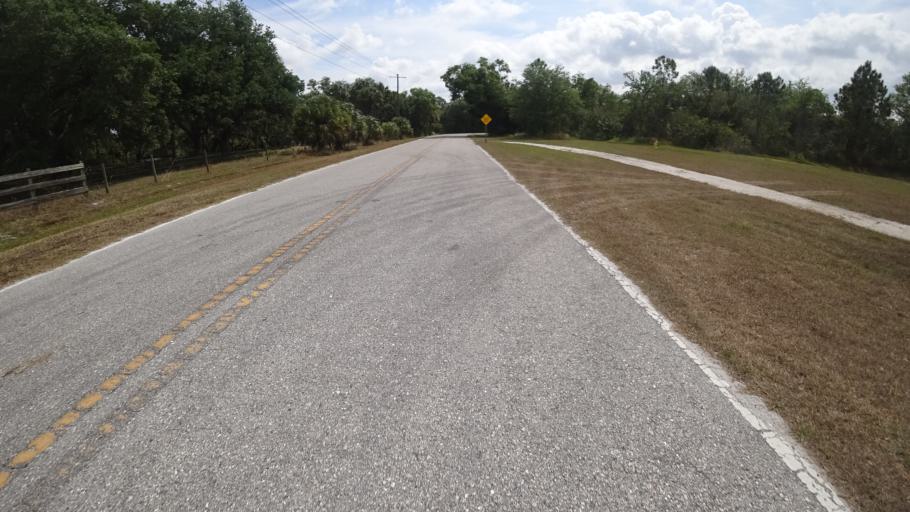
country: US
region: Florida
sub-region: Manatee County
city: Ellenton
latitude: 27.5355
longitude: -82.4018
